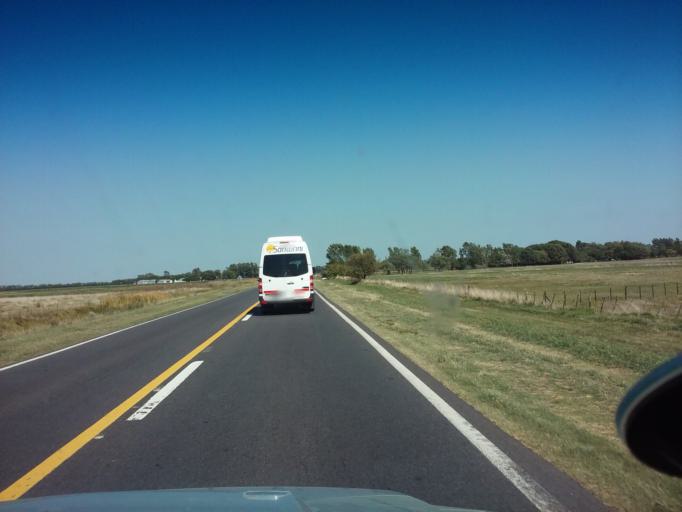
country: AR
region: Buenos Aires
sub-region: Partido de Chivilcoy
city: Chivilcoy
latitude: -34.9559
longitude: -60.0254
